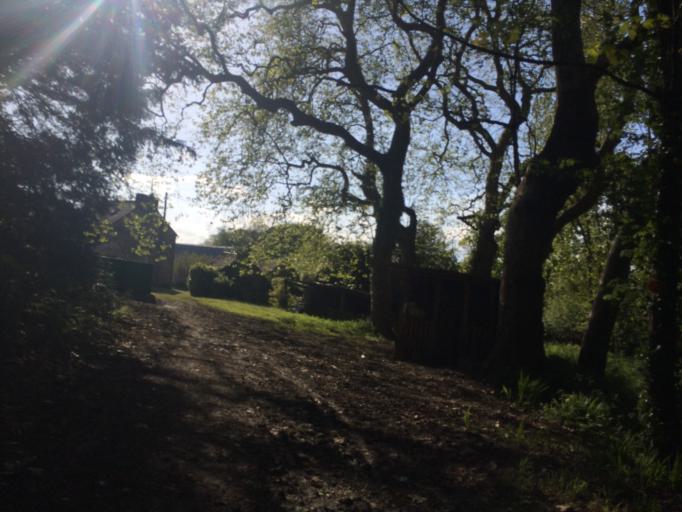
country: FR
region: Brittany
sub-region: Departement du Finistere
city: Daoulas
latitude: 48.3586
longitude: -4.2528
